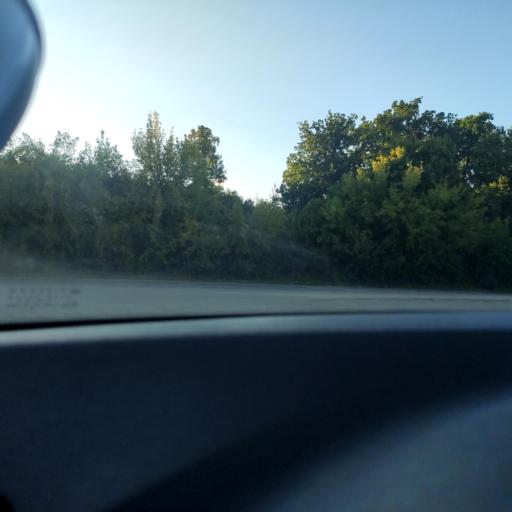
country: RU
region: Samara
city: Novosemeykino
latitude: 53.3357
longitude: 50.3211
